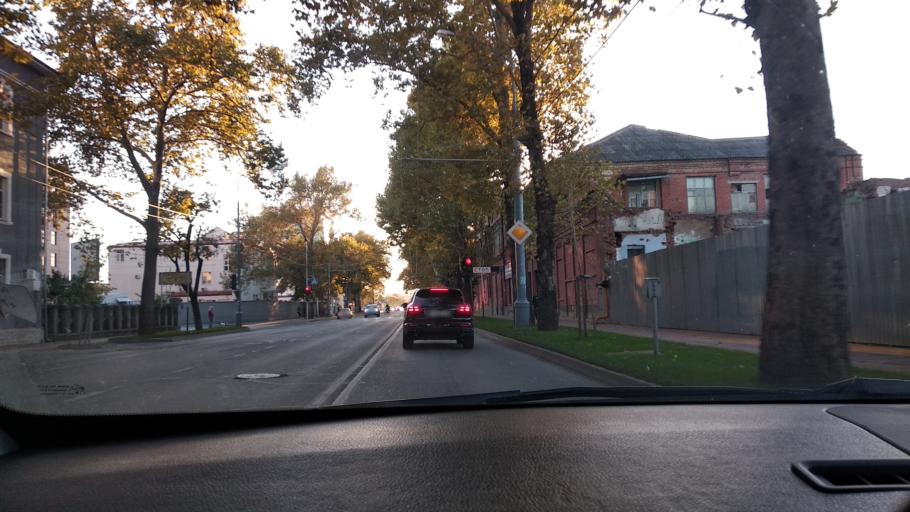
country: RU
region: Krasnodarskiy
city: Krasnodar
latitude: 45.0143
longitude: 38.9837
